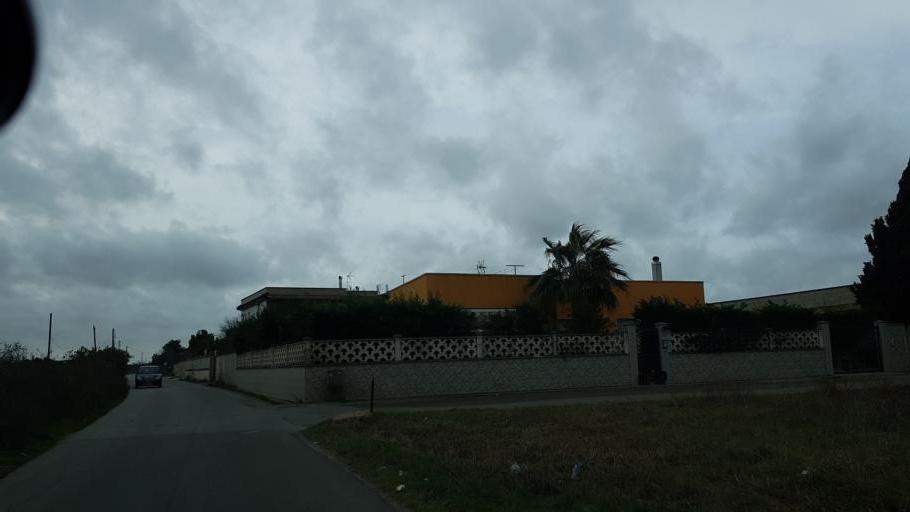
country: IT
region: Apulia
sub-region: Provincia di Brindisi
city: Brindisi
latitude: 40.6142
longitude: 17.9274
